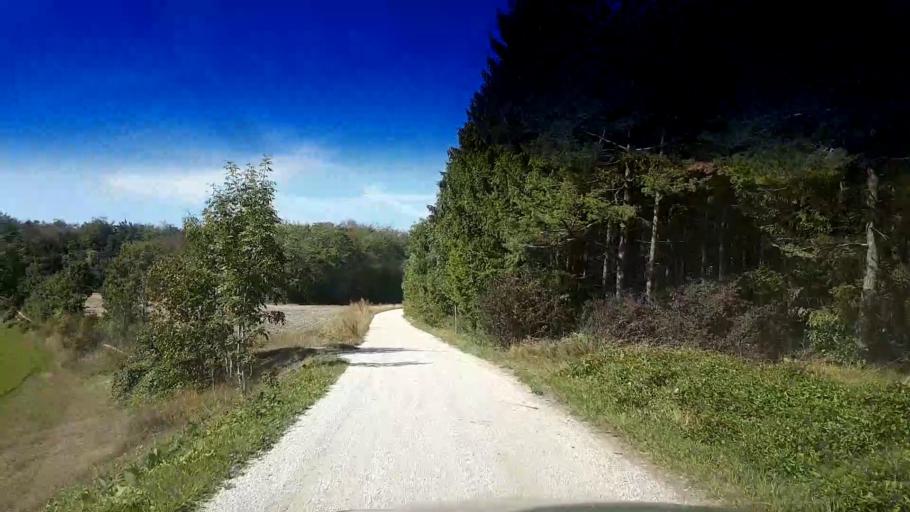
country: DE
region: Bavaria
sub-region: Upper Franconia
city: Poxdorf
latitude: 49.8760
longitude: 11.0854
